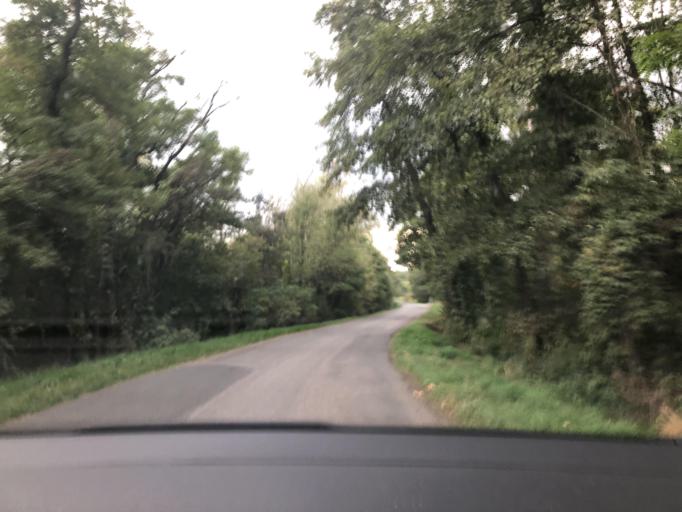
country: CZ
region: Central Bohemia
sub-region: Okres Kolin
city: Tynec nad Labem
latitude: 50.0516
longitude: 15.3822
